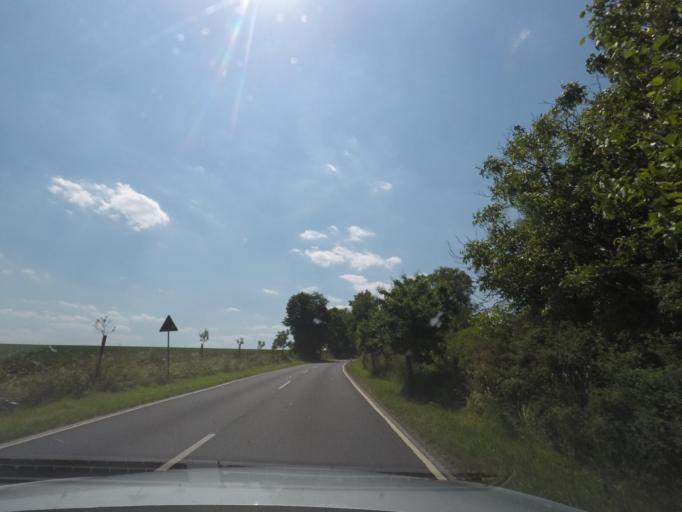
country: DE
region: Saxony-Anhalt
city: Haldensleben I
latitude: 52.2525
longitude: 11.4107
